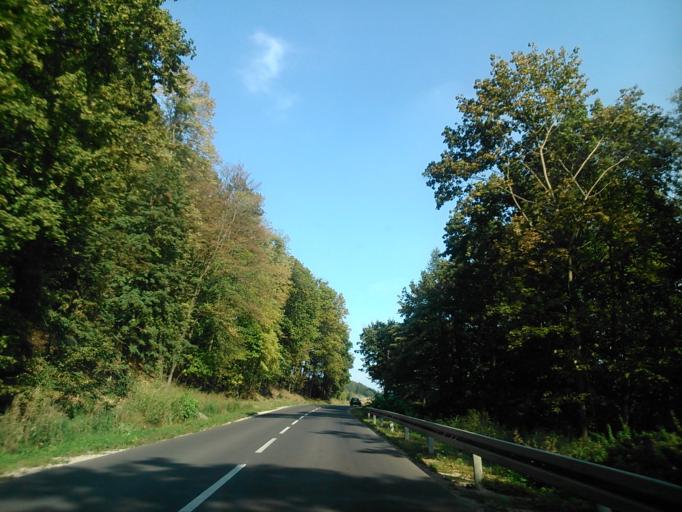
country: PL
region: Kujawsko-Pomorskie
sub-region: Powiat golubsko-dobrzynski
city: Golub-Dobrzyn
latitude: 53.1243
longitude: 19.0753
